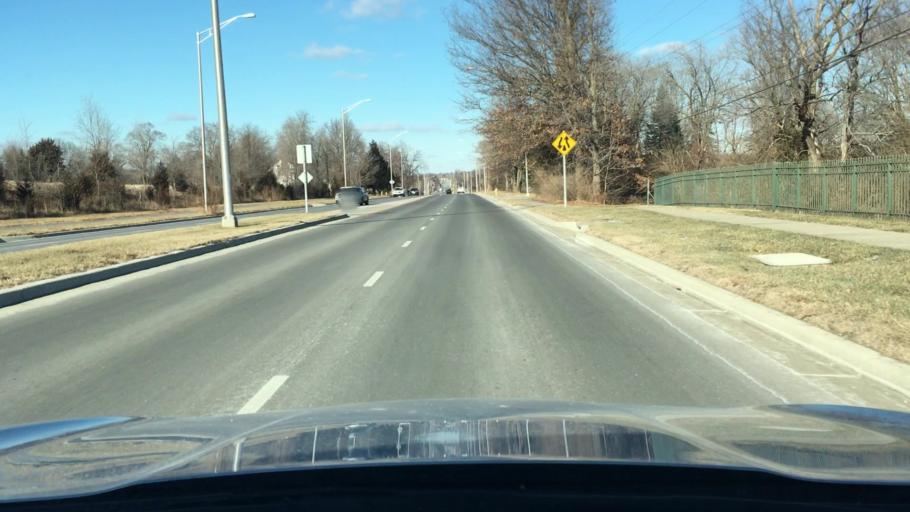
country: US
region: Missouri
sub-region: Jackson County
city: Lees Summit
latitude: 38.8929
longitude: -94.3963
